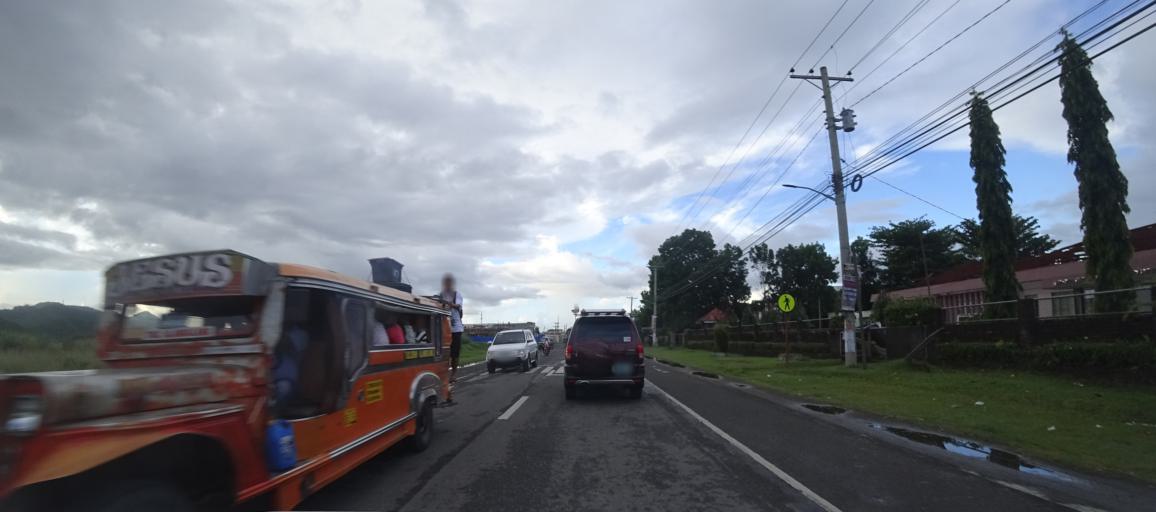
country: PH
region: Eastern Visayas
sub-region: Province of Leyte
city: Pawing
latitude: 11.1751
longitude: 125.0004
